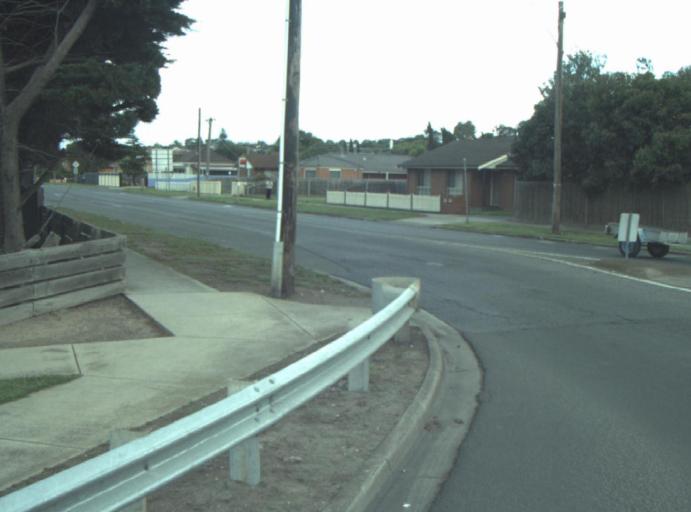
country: AU
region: Victoria
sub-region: Greater Geelong
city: Bell Park
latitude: -38.0985
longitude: 144.3341
